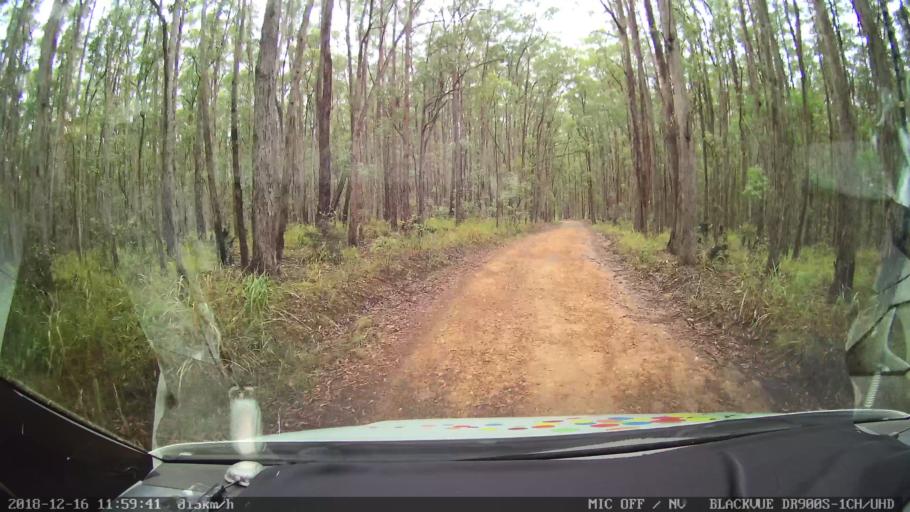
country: AU
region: New South Wales
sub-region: Tenterfield Municipality
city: Carrolls Creek
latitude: -28.9267
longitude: 152.3152
